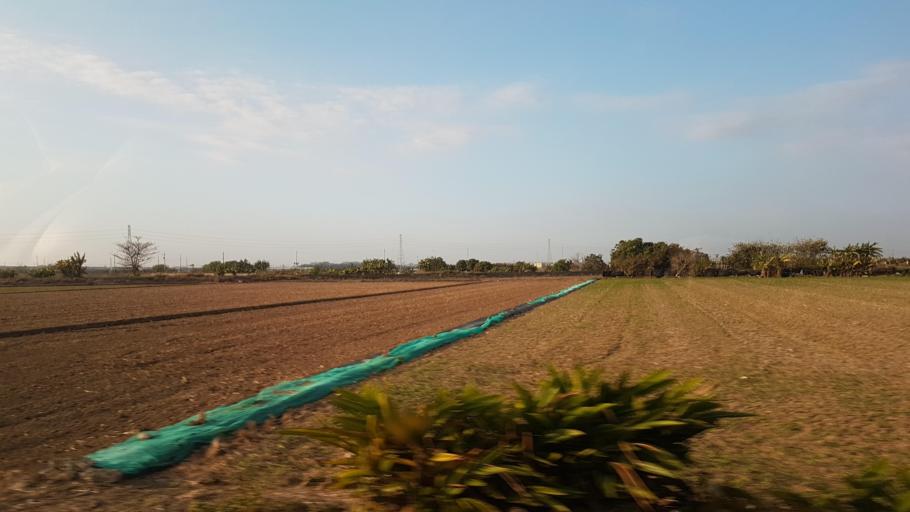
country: TW
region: Taiwan
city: Xinying
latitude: 23.3424
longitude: 120.3426
